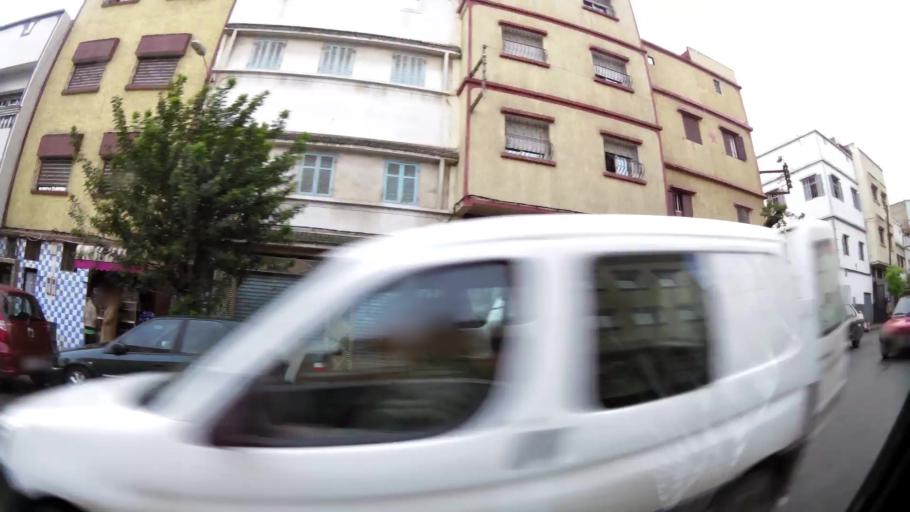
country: MA
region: Grand Casablanca
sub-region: Casablanca
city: Casablanca
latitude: 33.5506
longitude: -7.5766
